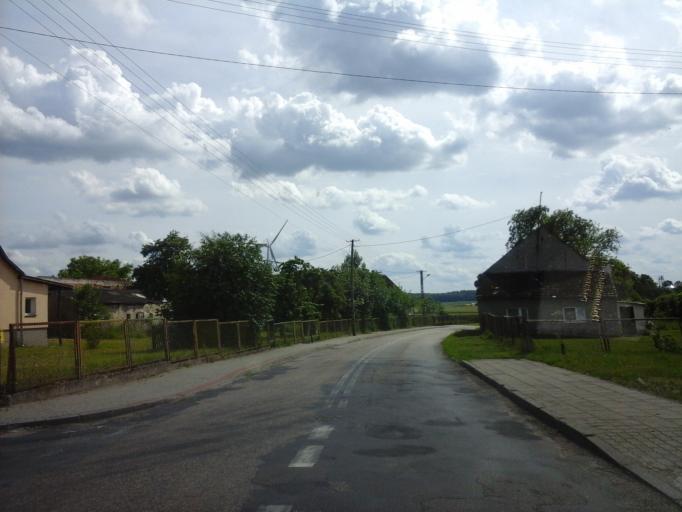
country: PL
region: West Pomeranian Voivodeship
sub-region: Powiat swidwinski
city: Swidwin
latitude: 53.7130
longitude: 15.7134
